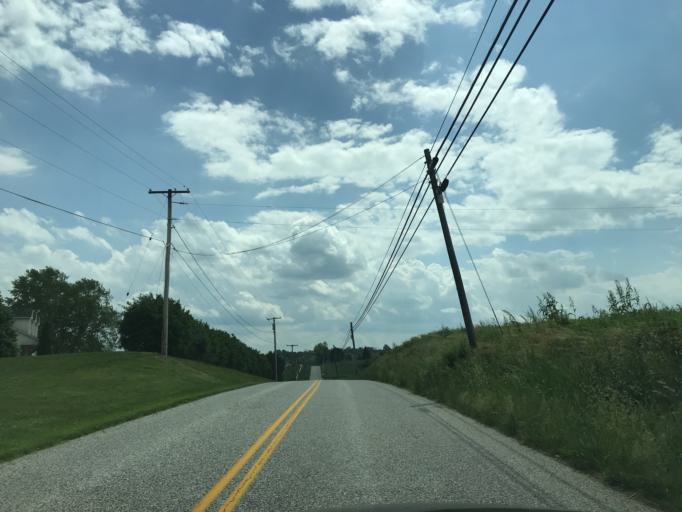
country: US
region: Maryland
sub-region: Harford County
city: Bel Air North
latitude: 39.6015
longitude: -76.3753
